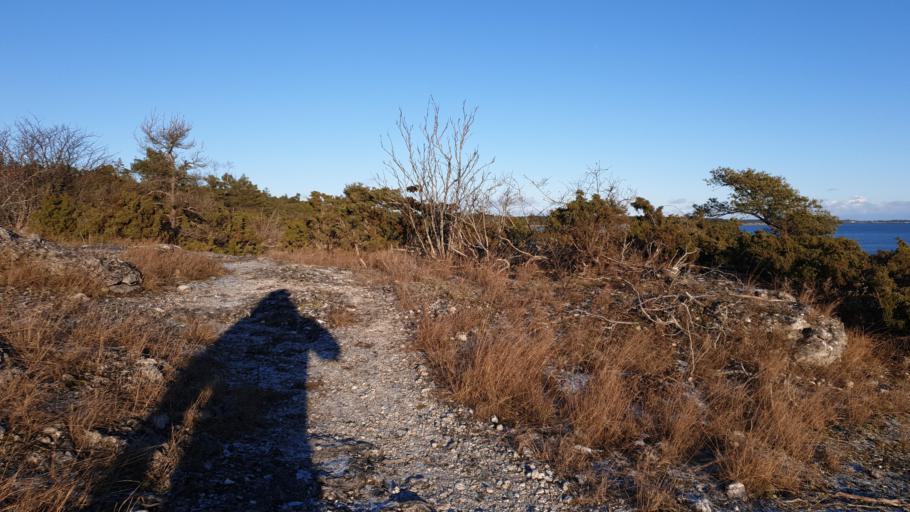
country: SE
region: Gotland
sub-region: Gotland
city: Slite
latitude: 57.3732
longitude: 18.8113
